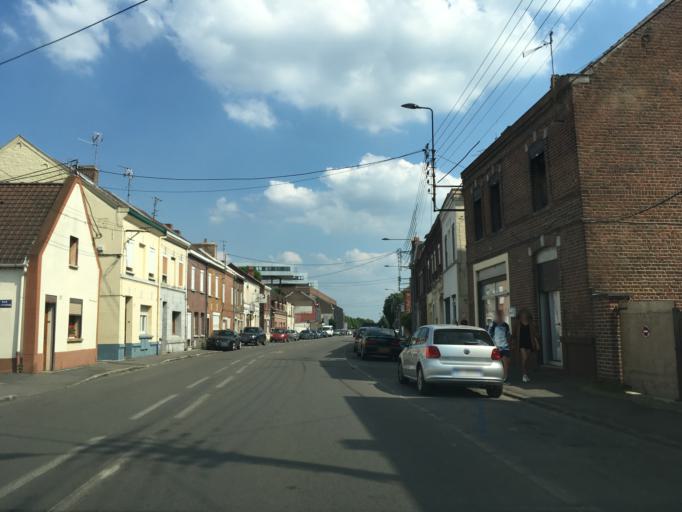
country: FR
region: Nord-Pas-de-Calais
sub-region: Departement du Nord
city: Petite-Foret
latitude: 50.3617
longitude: 3.4955
